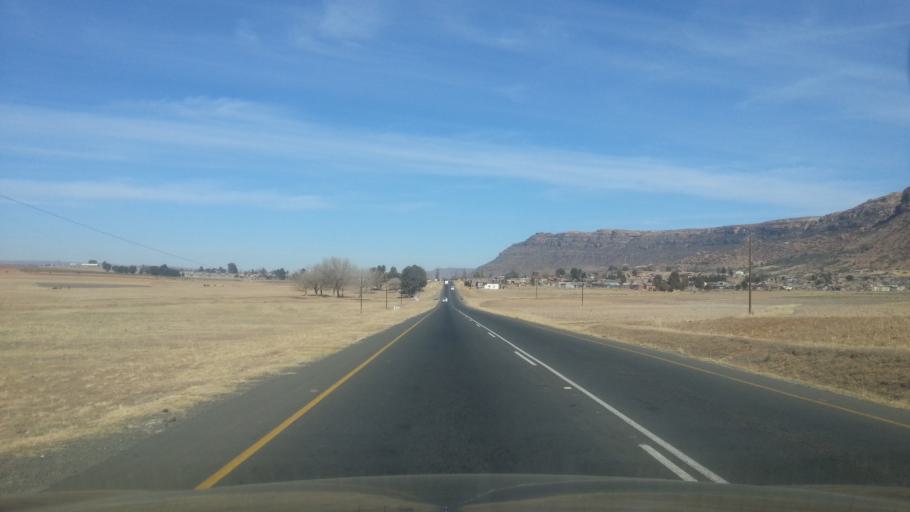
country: LS
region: Maseru
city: Maseru
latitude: -29.4750
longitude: 27.5310
